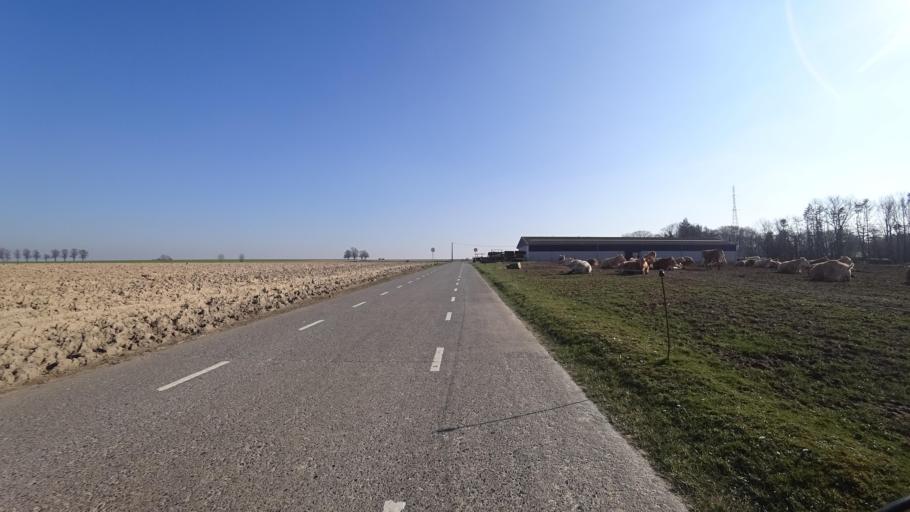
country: BE
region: Wallonia
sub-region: Province du Brabant Wallon
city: Court-Saint-Etienne
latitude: 50.6138
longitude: 4.5760
